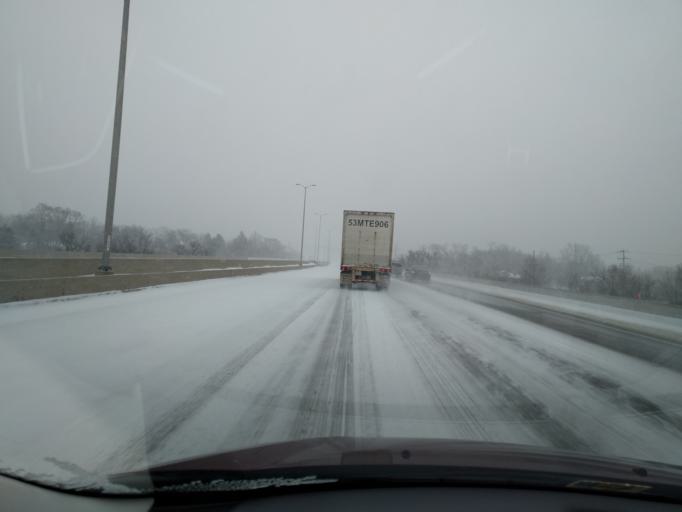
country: US
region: Wisconsin
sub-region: Waukesha County
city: Butler
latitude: 43.1353
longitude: -88.0326
